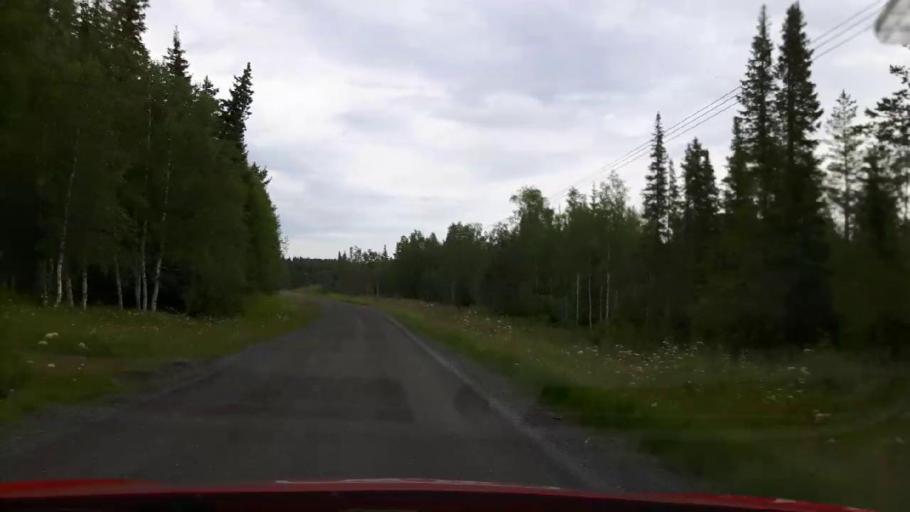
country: SE
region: Jaemtland
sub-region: Stroemsunds Kommun
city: Stroemsund
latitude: 63.4720
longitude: 15.2901
